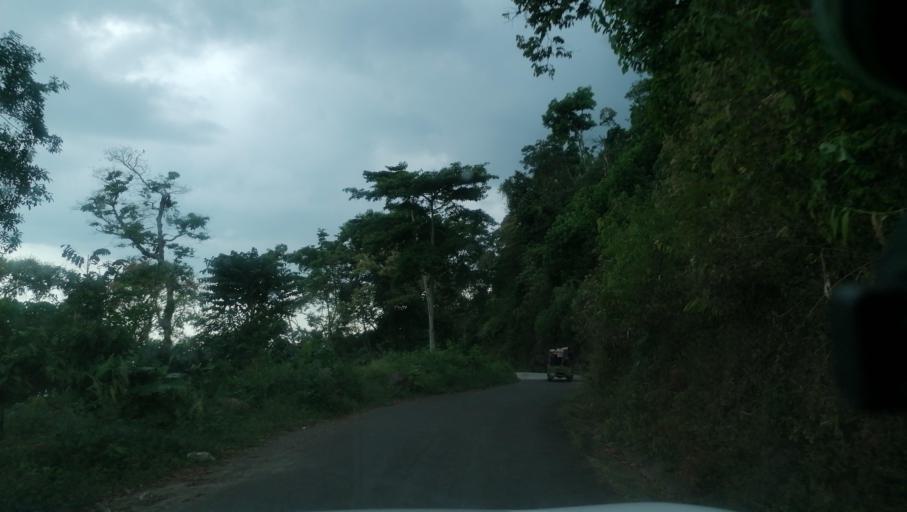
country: MX
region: Chiapas
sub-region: Cacahoatan
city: Benito Juarez
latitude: 15.0711
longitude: -92.1746
